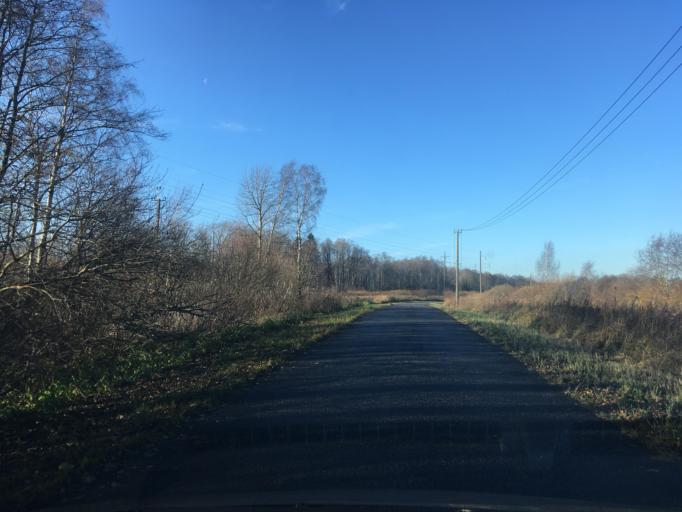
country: EE
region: Harju
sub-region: Maardu linn
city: Maardu
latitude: 59.4764
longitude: 25.1167
